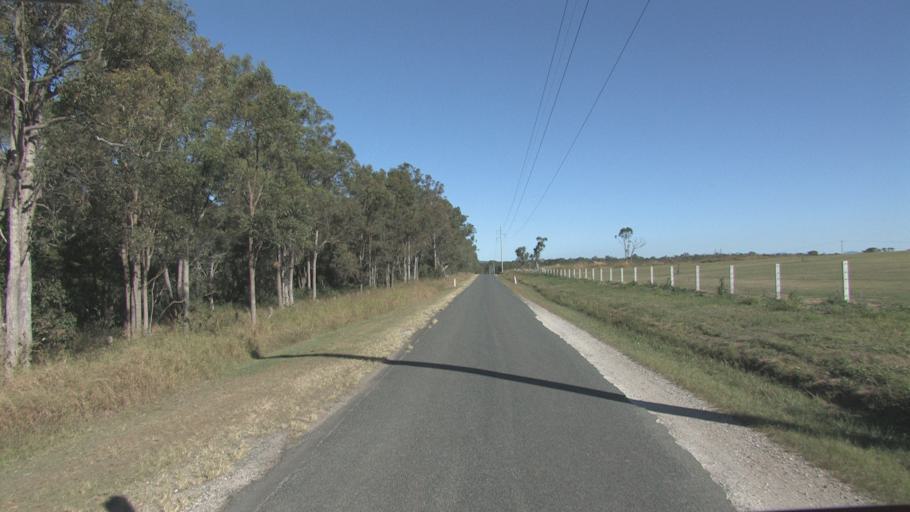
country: AU
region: Queensland
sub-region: Logan
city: Chambers Flat
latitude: -27.7720
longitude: 153.0596
